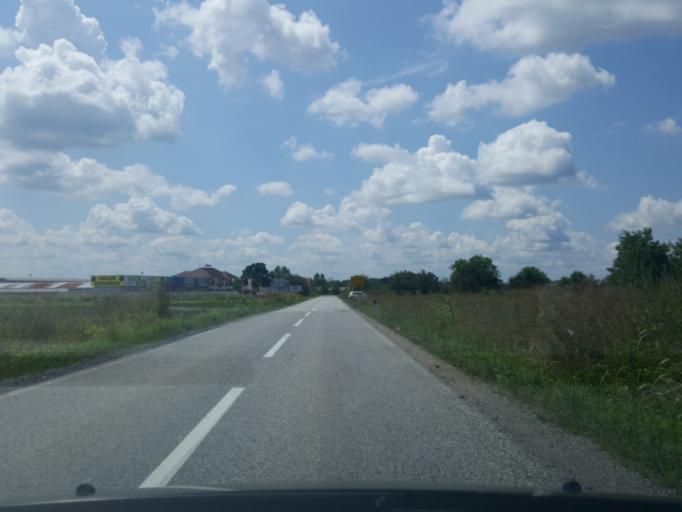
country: RS
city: Metkovic
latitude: 44.8439
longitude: 19.5183
